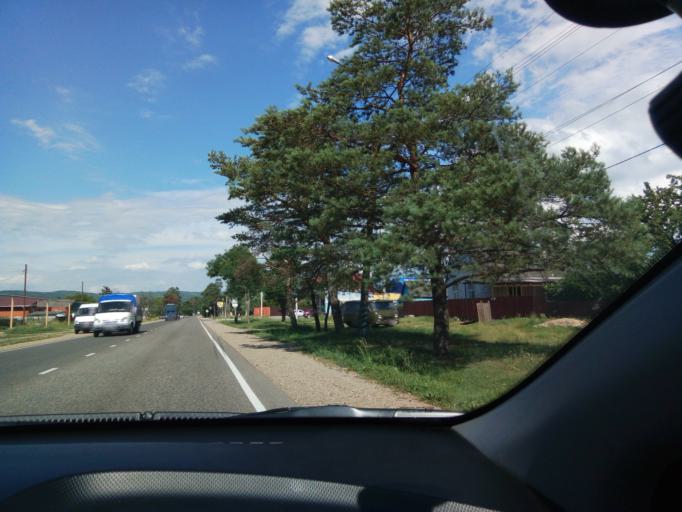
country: RU
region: Krasnodarskiy
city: Apsheronsk
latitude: 44.4640
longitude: 39.7016
